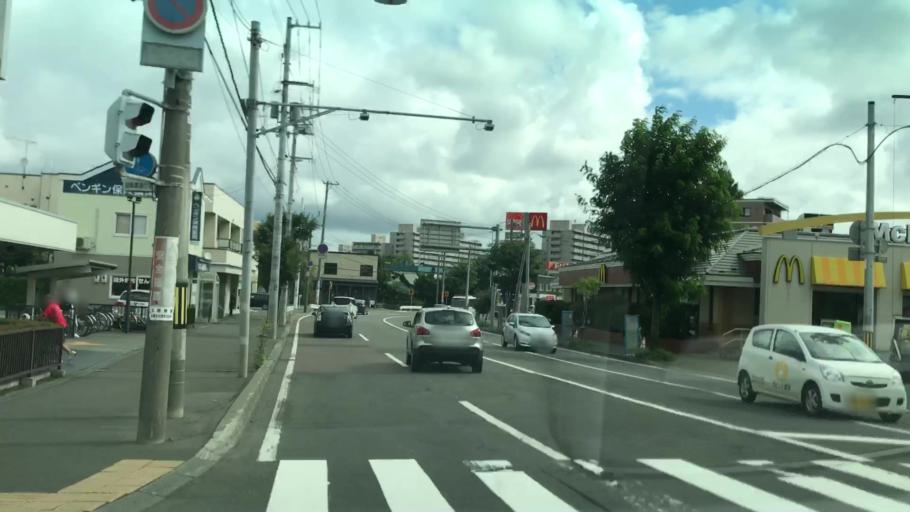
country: JP
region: Hokkaido
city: Sapporo
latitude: 43.0875
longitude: 141.3274
